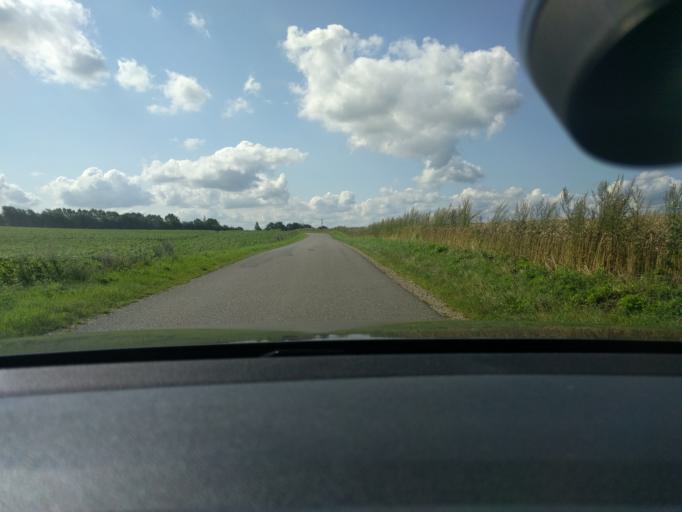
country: DK
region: Central Jutland
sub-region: Viborg Kommune
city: Viborg
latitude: 56.5062
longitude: 9.5066
